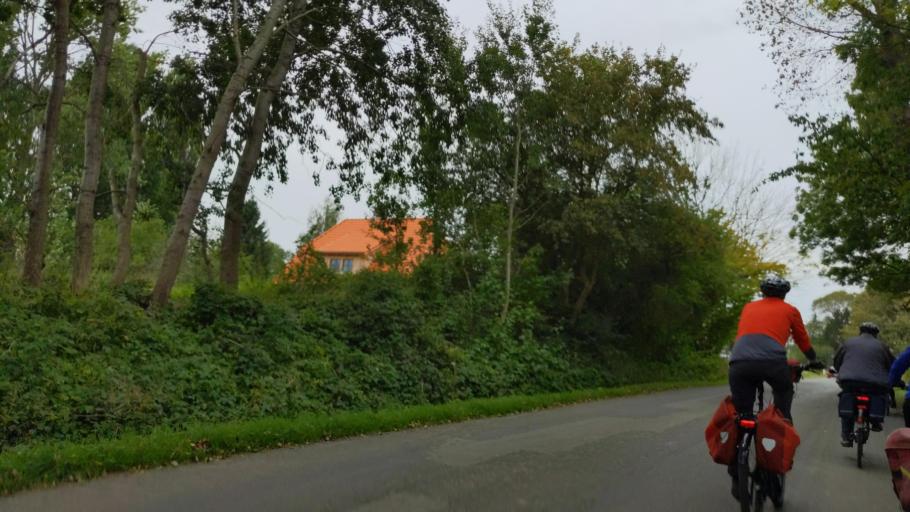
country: DE
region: Mecklenburg-Vorpommern
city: Schlagsdorf
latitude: 53.7576
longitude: 10.8278
